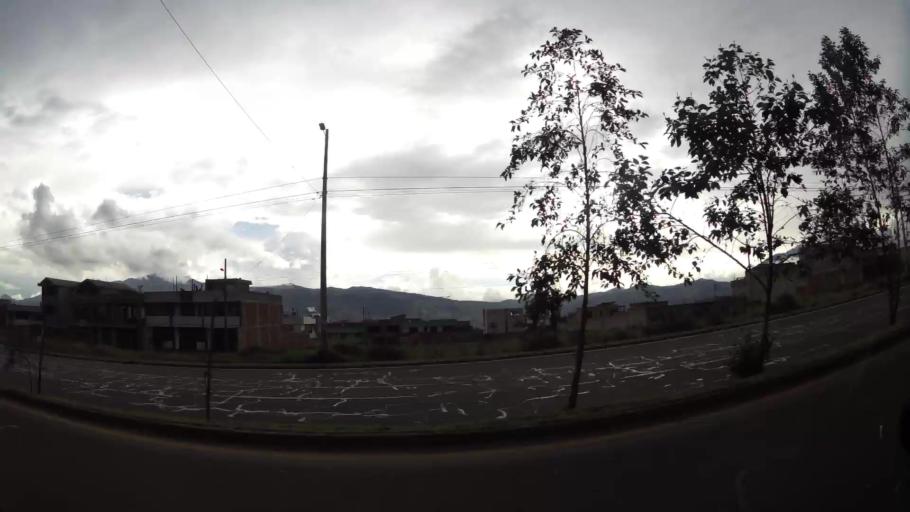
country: EC
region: Pichincha
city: Quito
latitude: -0.2975
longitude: -78.5206
